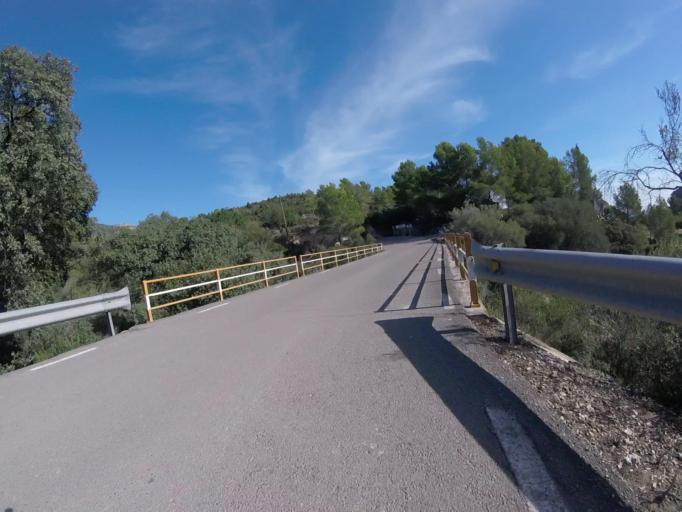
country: ES
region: Valencia
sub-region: Provincia de Castello
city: Sarratella
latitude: 40.2721
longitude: 0.0383
